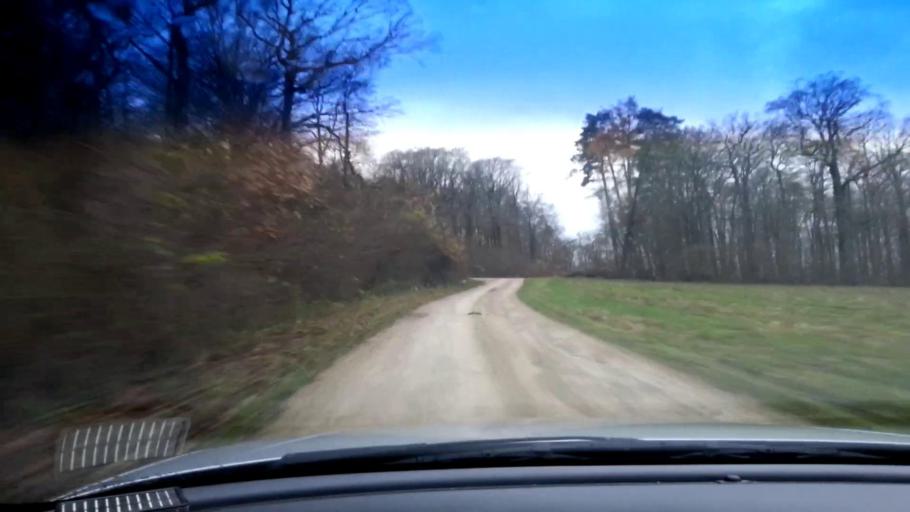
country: DE
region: Bavaria
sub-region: Upper Franconia
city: Schesslitz
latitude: 49.9442
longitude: 11.0265
